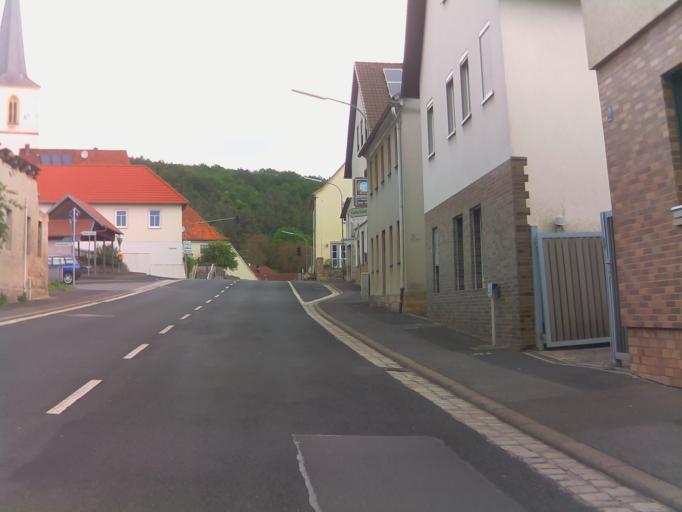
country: DE
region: Bavaria
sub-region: Regierungsbezirk Unterfranken
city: Stockheim
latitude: 50.4632
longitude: 10.3191
